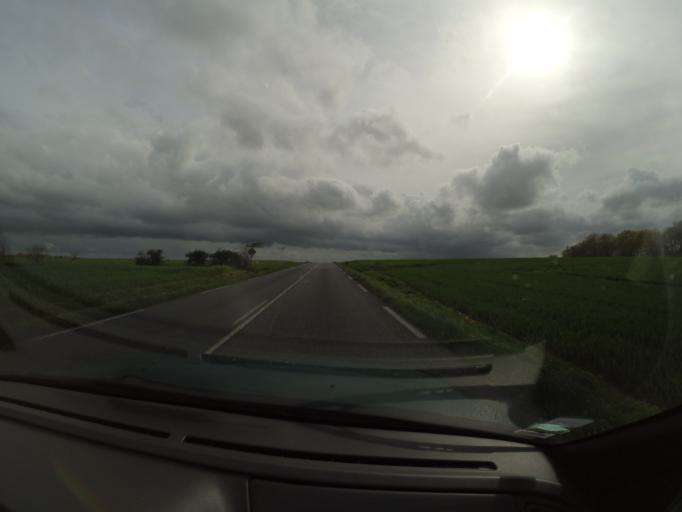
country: FR
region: Pays de la Loire
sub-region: Departement de Maine-et-Loire
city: Landemont
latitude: 47.2532
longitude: -1.2060
